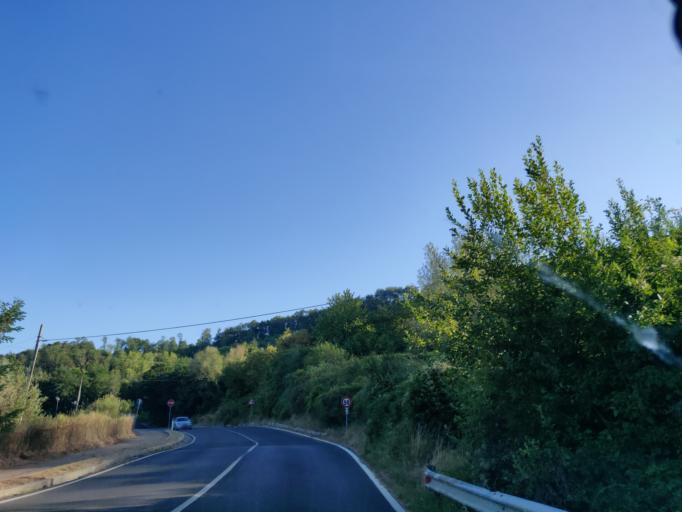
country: IT
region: Tuscany
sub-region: Provincia di Siena
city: Piancastagnaio
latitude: 42.8634
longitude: 11.6786
